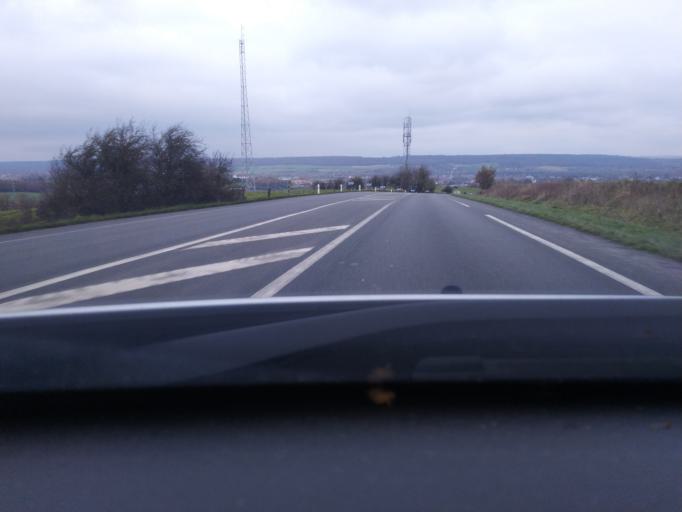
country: FR
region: Nord-Pas-de-Calais
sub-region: Departement du Pas-de-Calais
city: Hesdin
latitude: 50.3541
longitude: 2.0346
